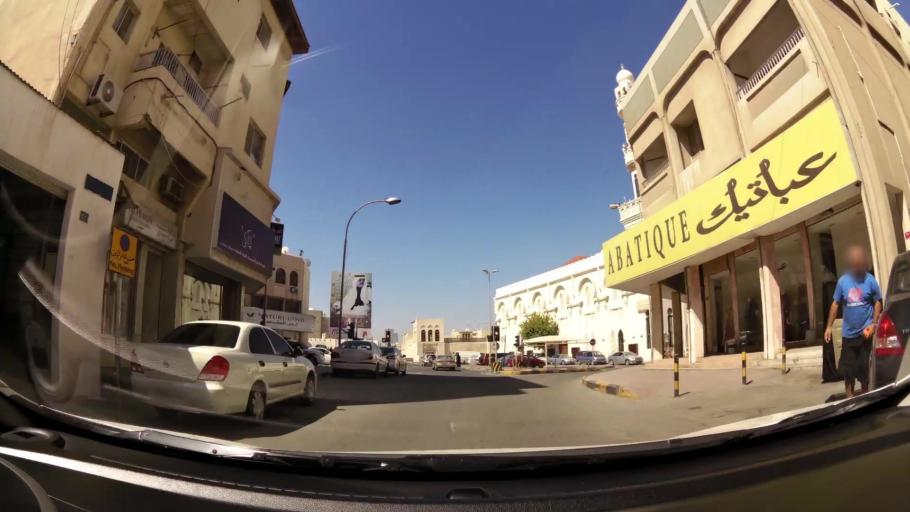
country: BH
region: Muharraq
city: Al Muharraq
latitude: 26.2539
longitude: 50.6140
